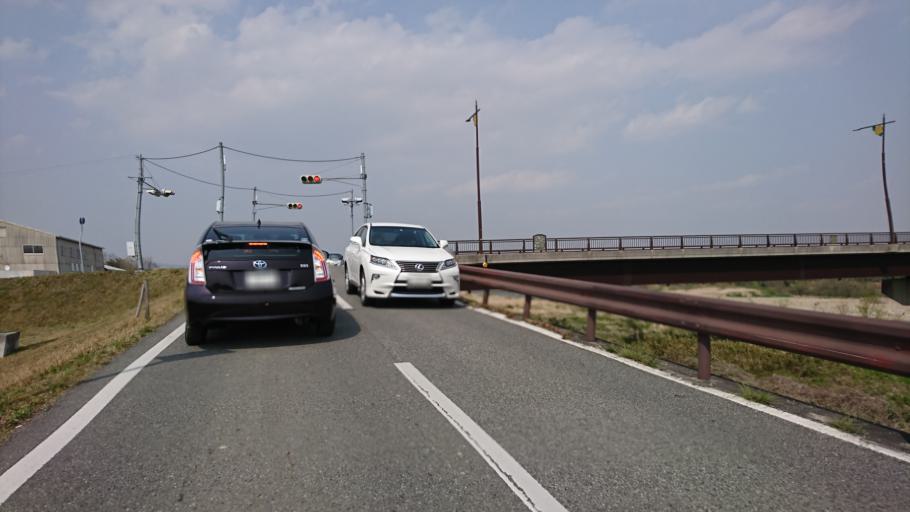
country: JP
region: Hyogo
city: Ono
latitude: 34.8777
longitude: 134.9256
